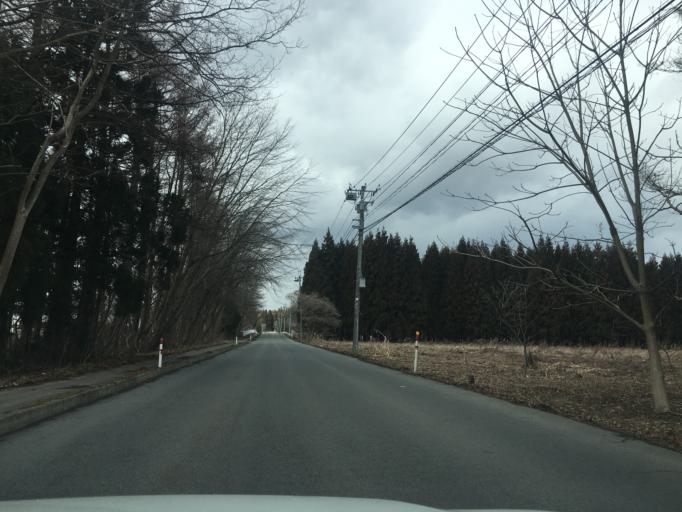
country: JP
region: Akita
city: Takanosu
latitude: 40.1816
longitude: 140.3437
